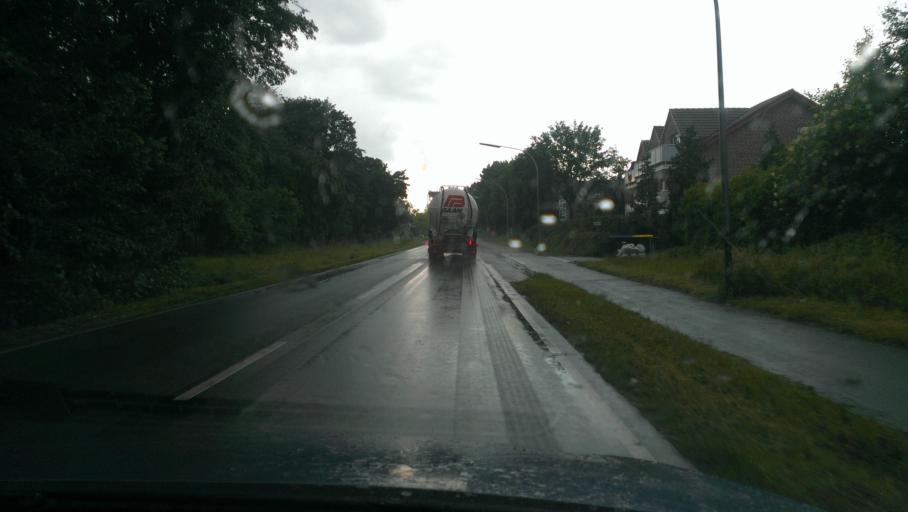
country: DE
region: North Rhine-Westphalia
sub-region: Regierungsbezirk Munster
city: Muenster
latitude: 51.9172
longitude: 7.6798
